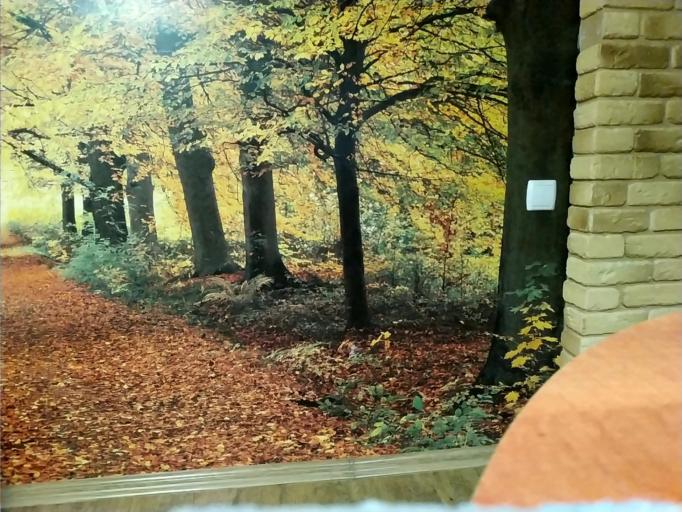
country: BY
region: Minsk
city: Plyeshchanitsy
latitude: 54.4269
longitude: 27.5935
